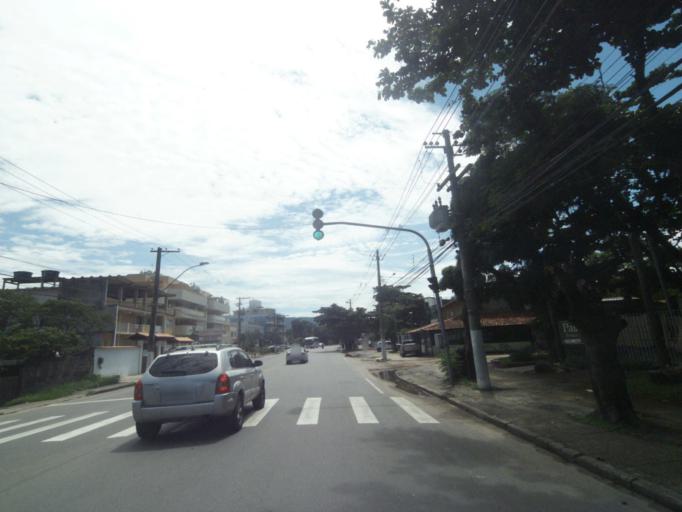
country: BR
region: Rio de Janeiro
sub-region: Niteroi
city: Niteroi
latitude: -22.9610
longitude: -43.0301
